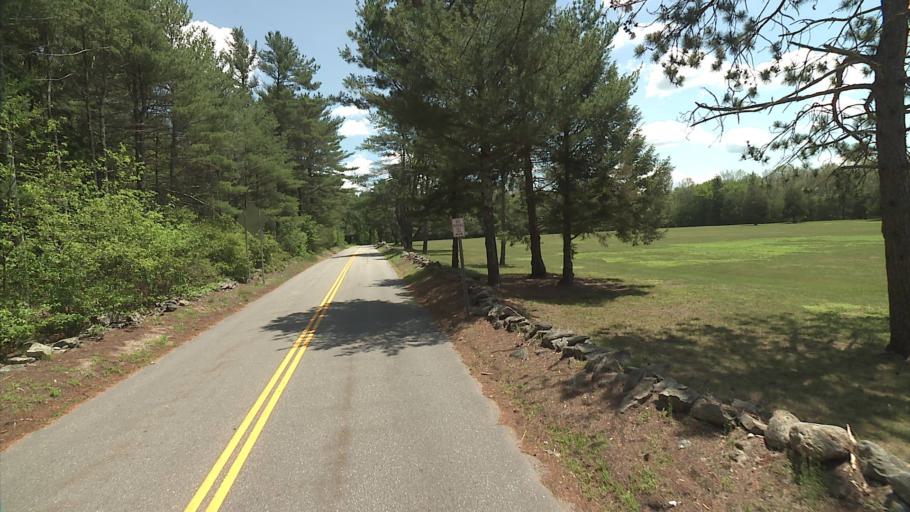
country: US
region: Connecticut
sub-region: New London County
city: Jewett City
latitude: 41.6079
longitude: -71.9180
